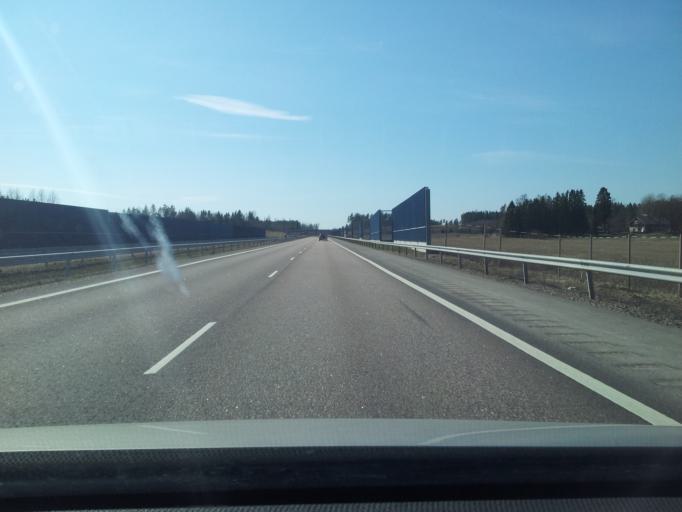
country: FI
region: Kymenlaakso
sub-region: Kotka-Hamina
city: Broby
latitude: 60.4980
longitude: 26.6895
